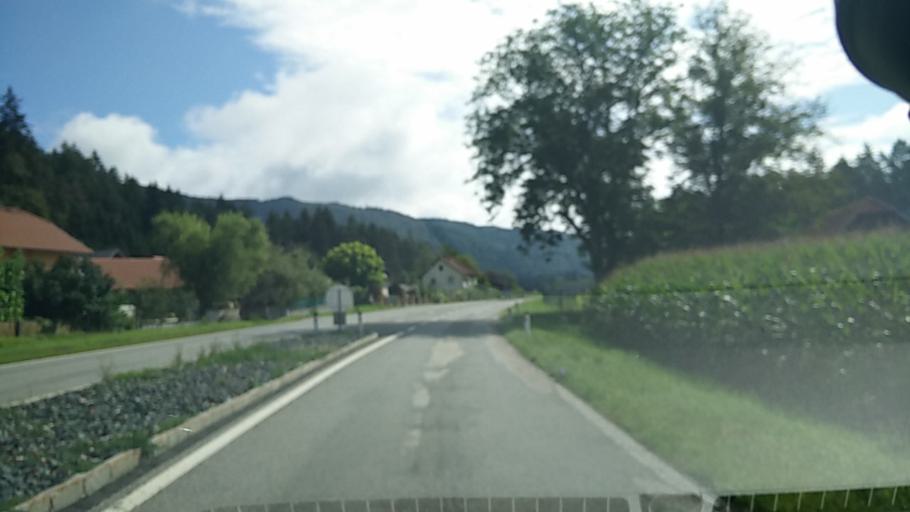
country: AT
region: Carinthia
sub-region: Politischer Bezirk Klagenfurt Land
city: Poggersdorf
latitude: 46.6560
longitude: 14.5291
